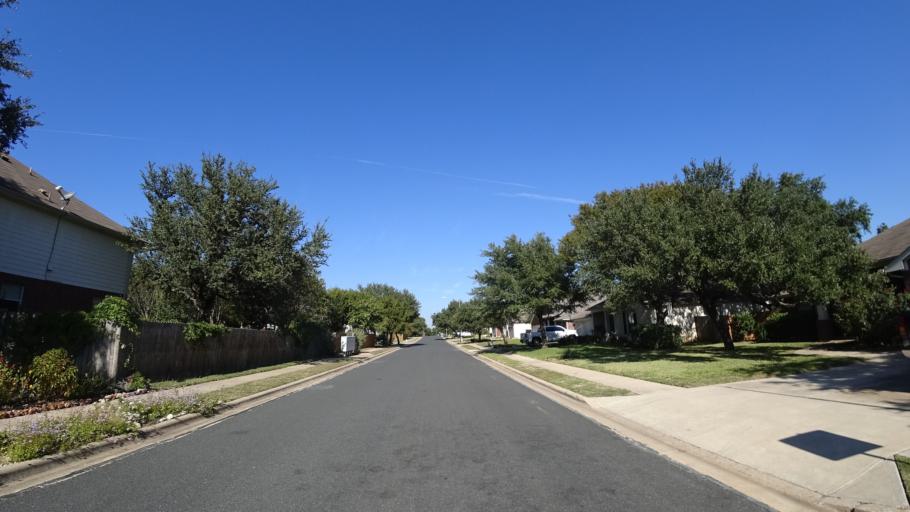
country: US
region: Texas
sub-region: Travis County
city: Shady Hollow
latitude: 30.1965
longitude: -97.8538
